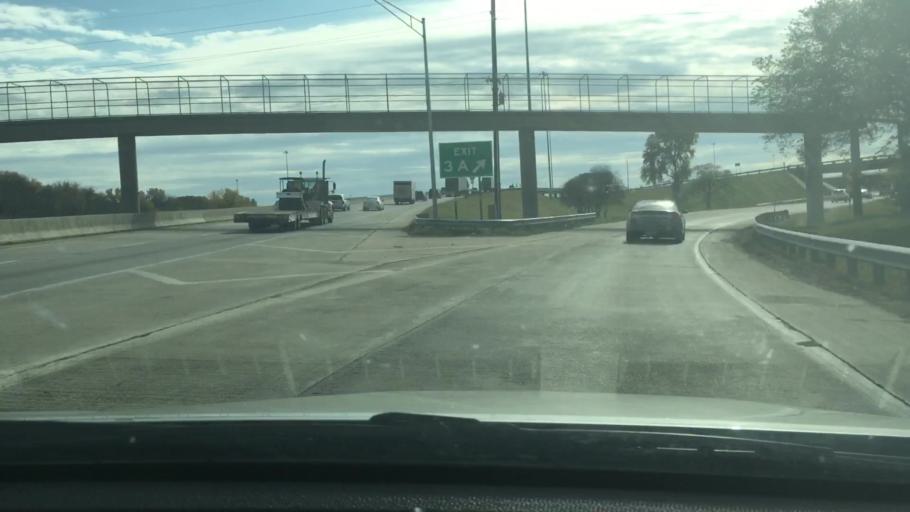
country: US
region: Kansas
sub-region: Sedgwick County
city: Wichita
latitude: 37.6428
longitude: -97.3085
